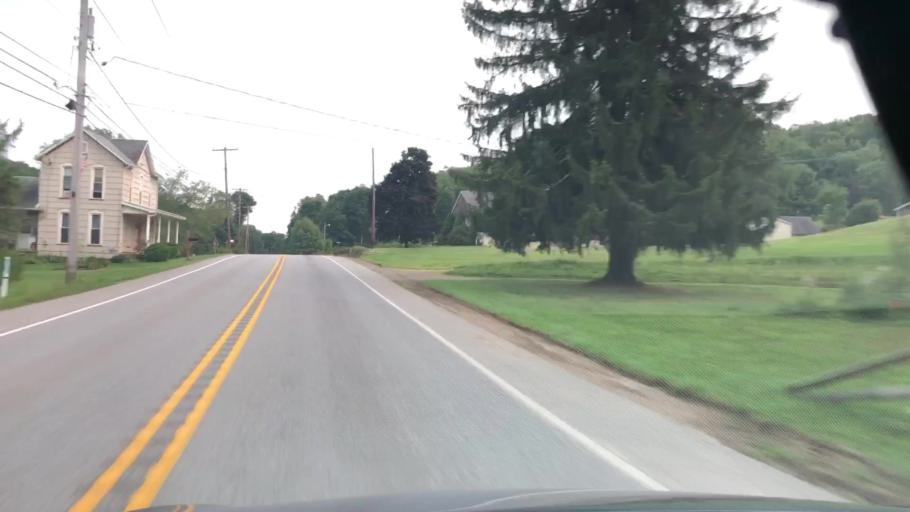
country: US
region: Pennsylvania
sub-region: Venango County
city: Hasson Heights
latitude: 41.5045
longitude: -79.7026
